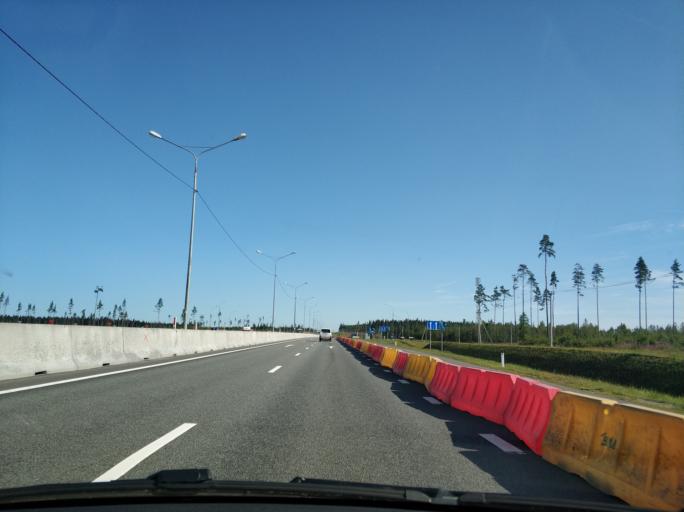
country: RU
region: Leningrad
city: Sosnovo
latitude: 60.4733
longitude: 30.1960
